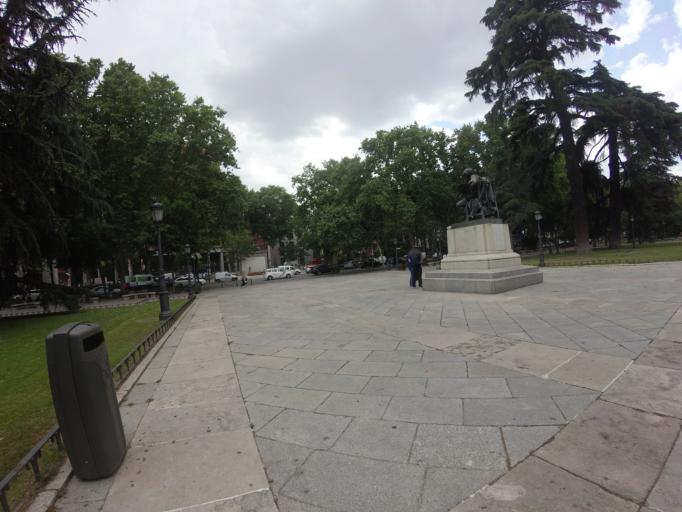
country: ES
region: Madrid
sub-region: Provincia de Madrid
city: Retiro
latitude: 40.4137
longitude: -3.6927
